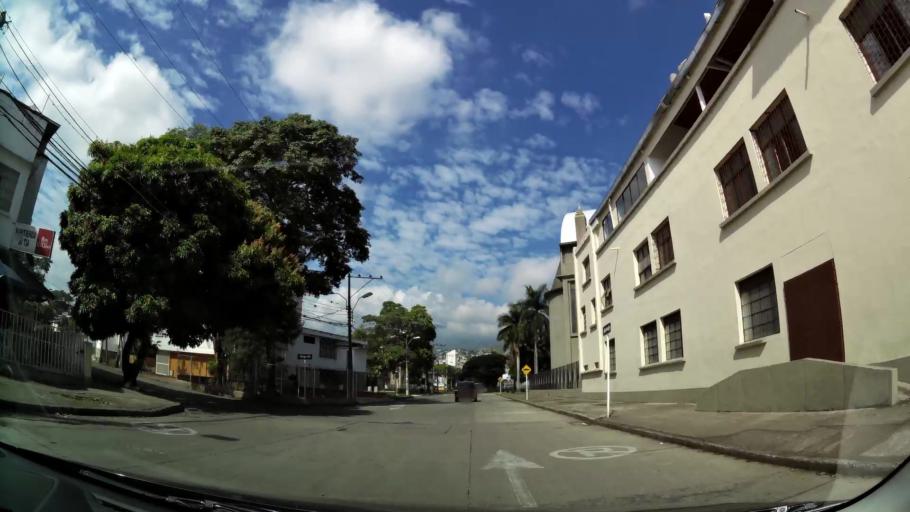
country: CO
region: Valle del Cauca
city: Cali
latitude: 3.4253
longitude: -76.5385
